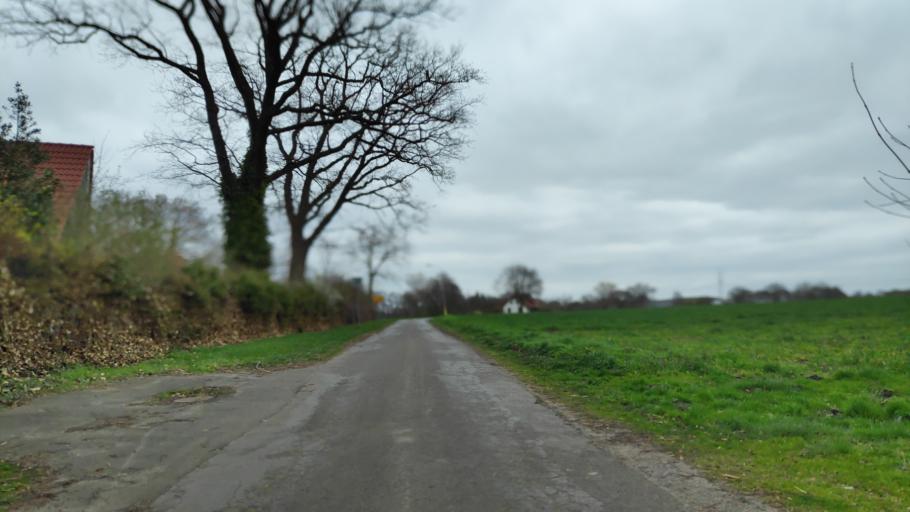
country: DE
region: North Rhine-Westphalia
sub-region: Regierungsbezirk Detmold
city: Minden
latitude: 52.3561
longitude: 8.8606
